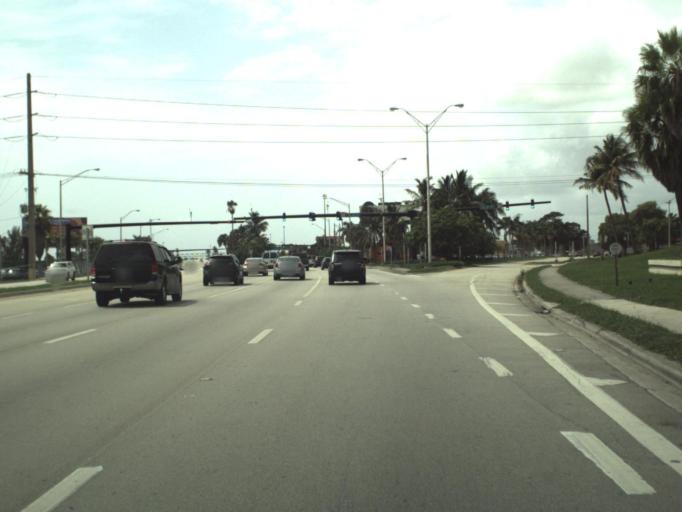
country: US
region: Florida
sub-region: Broward County
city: Fort Lauderdale
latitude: 26.0901
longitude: -80.1366
